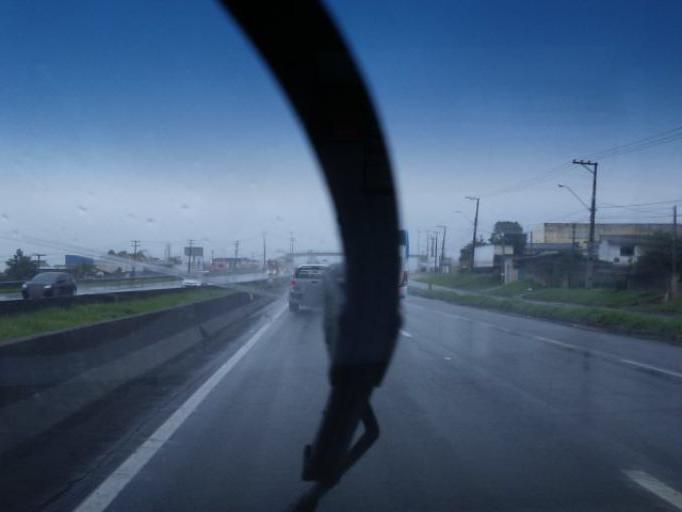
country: BR
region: Parana
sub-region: Sao Jose Dos Pinhais
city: Sao Jose dos Pinhais
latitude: -25.6131
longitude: -49.1710
